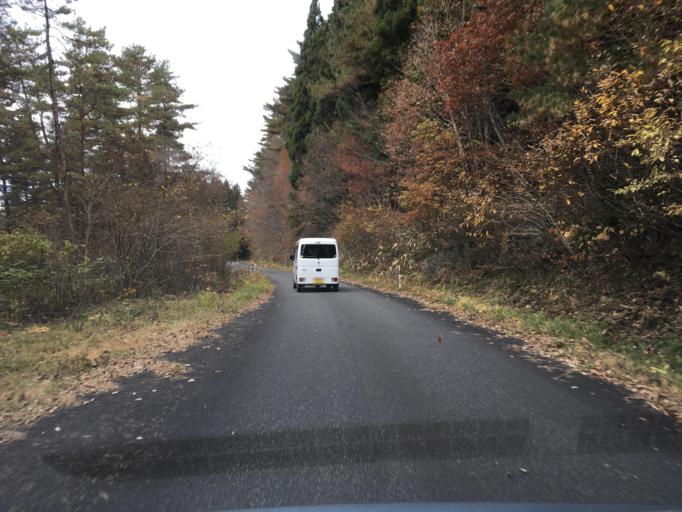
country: JP
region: Iwate
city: Mizusawa
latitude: 39.1253
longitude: 141.3210
